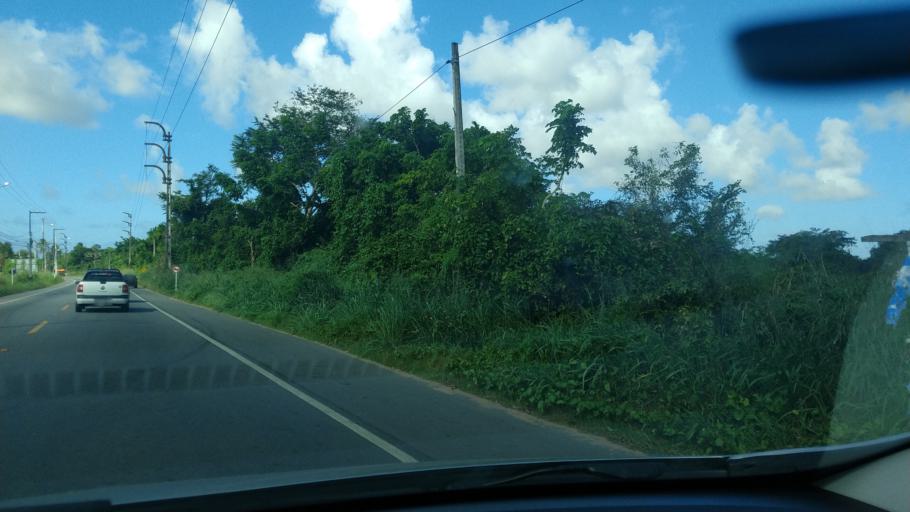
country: BR
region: Rio Grande do Norte
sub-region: Sao Goncalo Do Amarante
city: Sao Goncalo do Amarante
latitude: -5.7871
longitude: -35.2924
